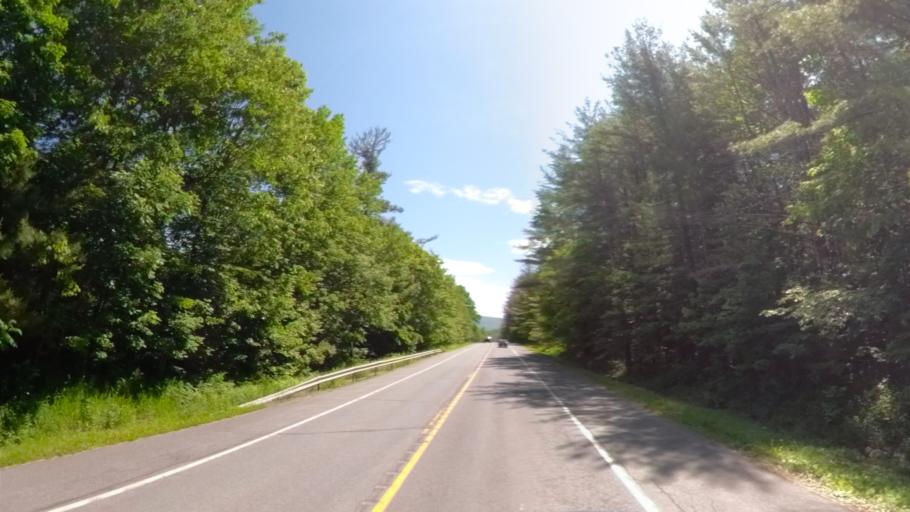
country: US
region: New York
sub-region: Ulster County
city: Shokan
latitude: 42.1152
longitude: -74.4164
